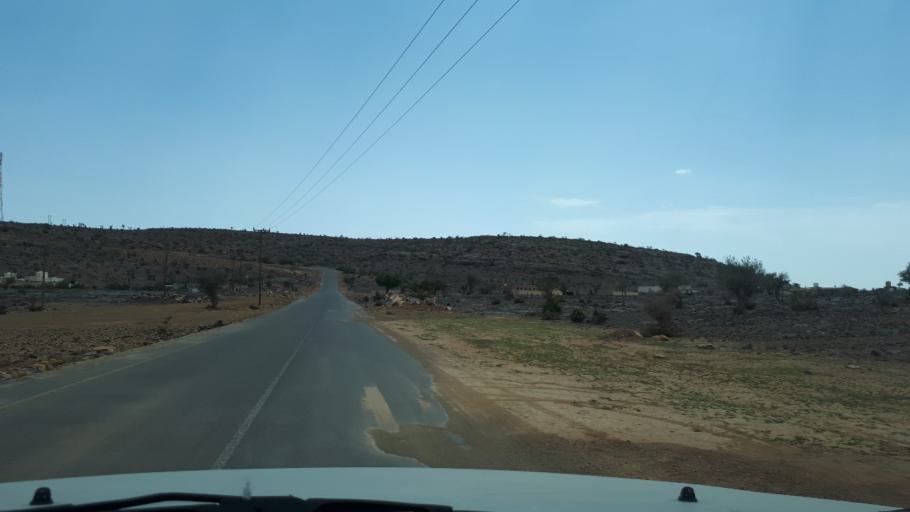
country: OM
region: Muhafazat ad Dakhiliyah
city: Bahla'
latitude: 23.2198
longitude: 57.2012
